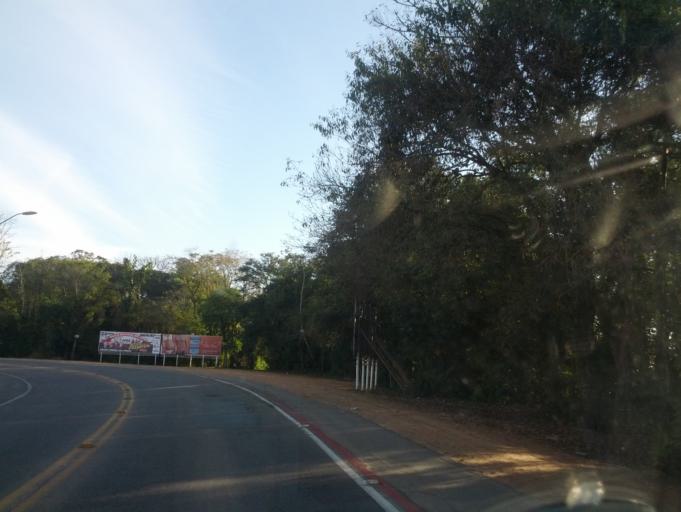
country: BR
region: Santa Catarina
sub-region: Indaial
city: Indaial
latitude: -26.8881
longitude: -49.1893
